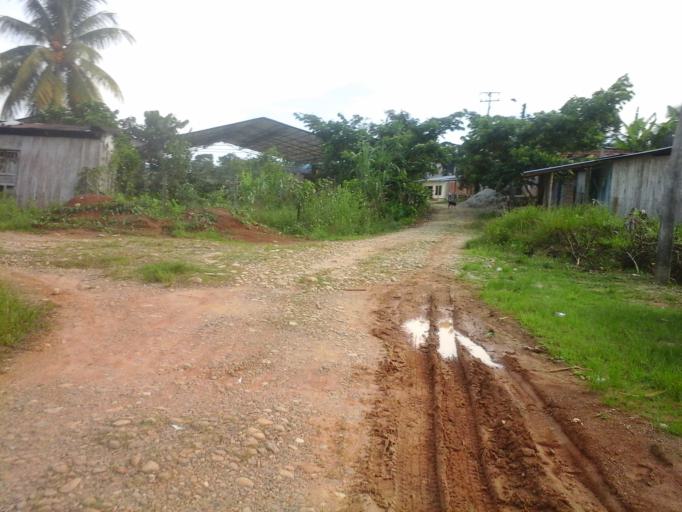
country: CO
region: Putumayo
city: Orito
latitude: 0.6493
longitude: -76.8239
